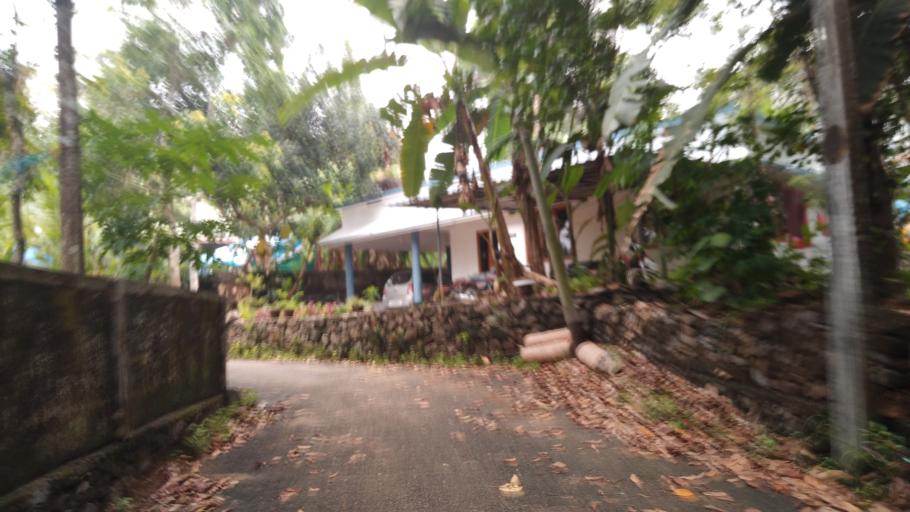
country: IN
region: Kerala
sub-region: Ernakulam
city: Kotamangalam
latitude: 10.1281
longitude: 76.5850
